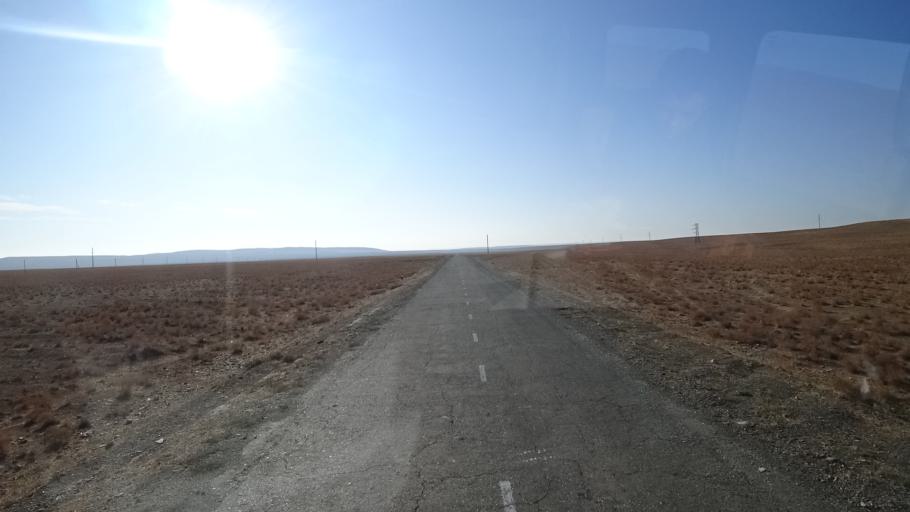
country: UZ
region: Navoiy
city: Karmana Shahri
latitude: 40.2688
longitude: 65.5222
